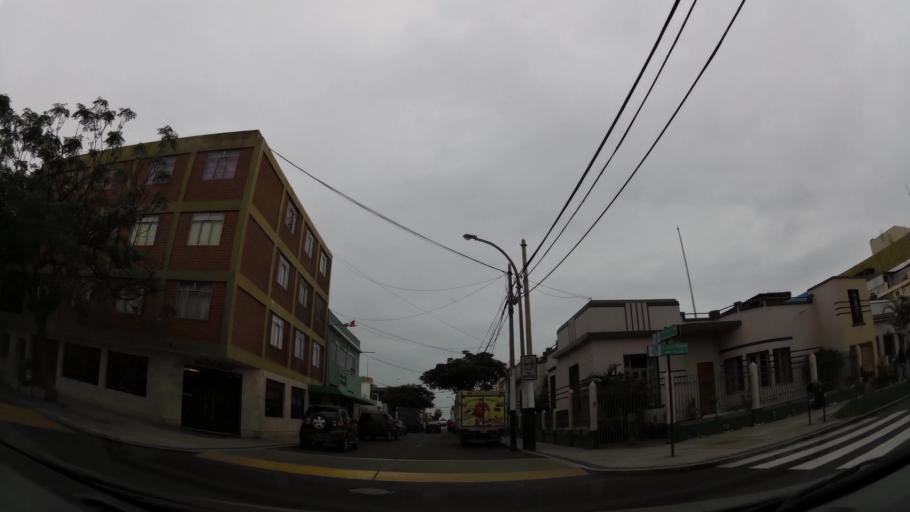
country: PE
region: Callao
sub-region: Callao
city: Callao
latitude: -12.0704
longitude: -77.1622
